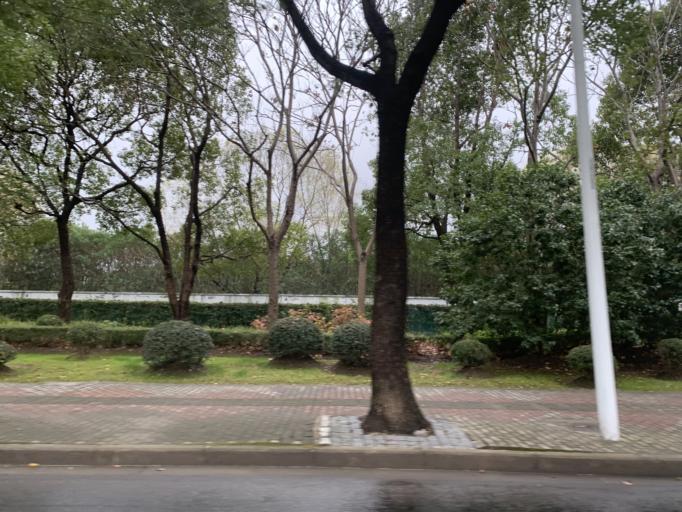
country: CN
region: Shanghai Shi
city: Huamu
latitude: 31.1958
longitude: 121.5404
